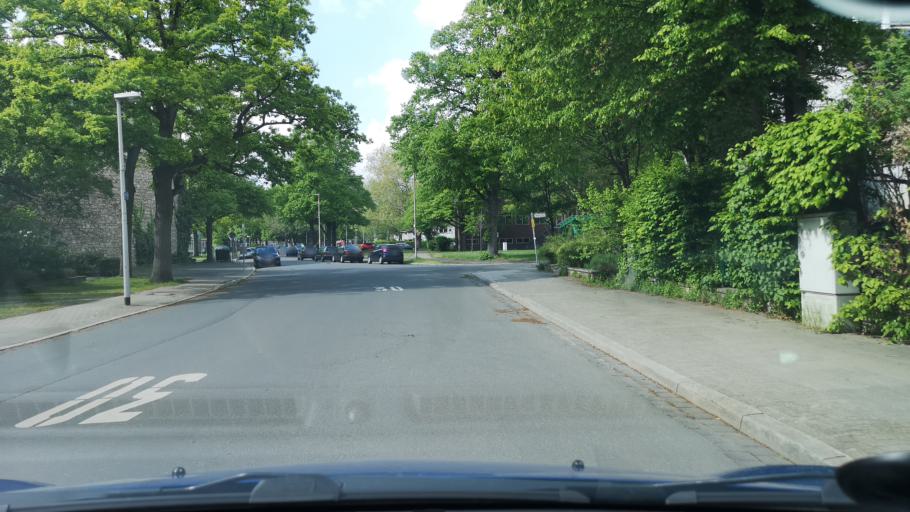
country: DE
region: Lower Saxony
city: Hannover
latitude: 52.3541
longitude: 9.7655
